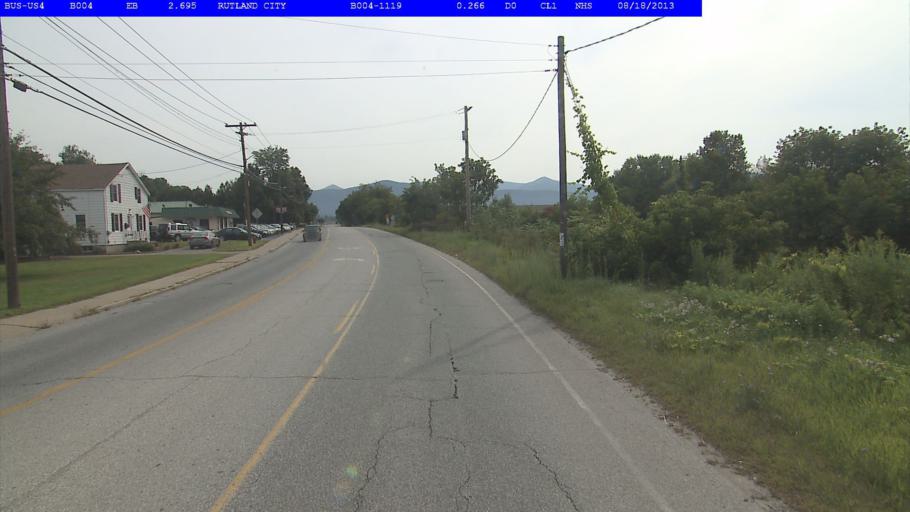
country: US
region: Vermont
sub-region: Rutland County
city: Rutland
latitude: 43.6042
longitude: -73.0019
